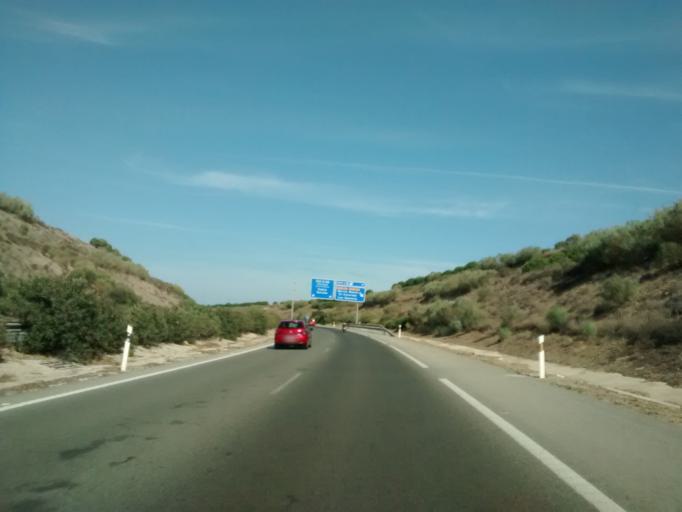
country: ES
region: Andalusia
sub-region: Provincia de Cadiz
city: Conil de la Frontera
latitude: 36.3427
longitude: -6.0510
